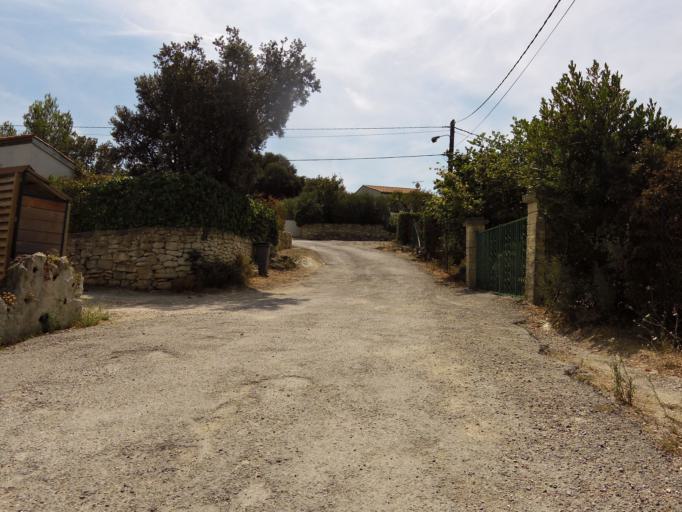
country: FR
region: Languedoc-Roussillon
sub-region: Departement du Gard
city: Villevieille
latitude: 43.7709
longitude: 4.1157
